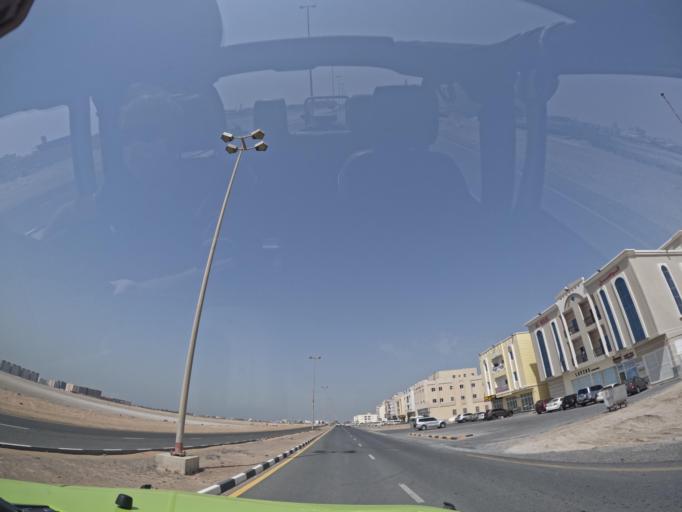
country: AE
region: Umm al Qaywayn
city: Umm al Qaywayn
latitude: 25.5157
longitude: 55.5562
